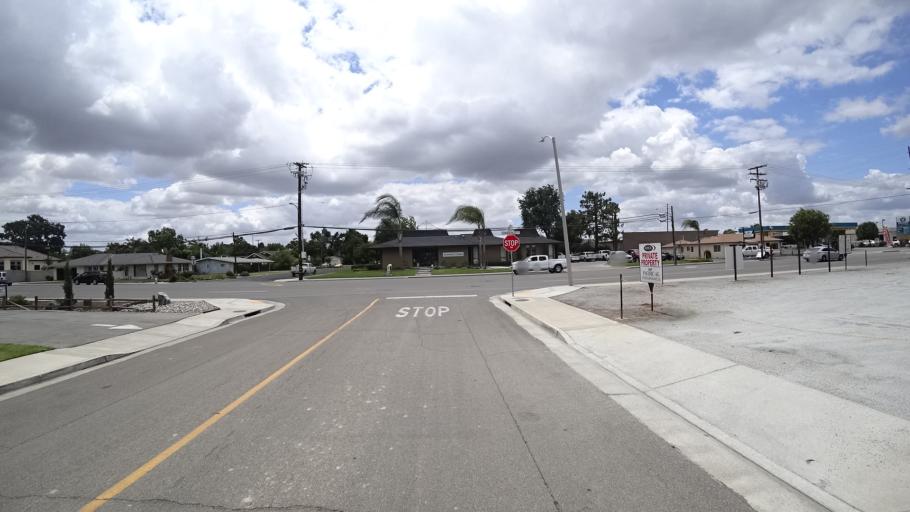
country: US
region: California
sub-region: Kings County
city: Hanford
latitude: 36.3429
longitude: -119.6540
